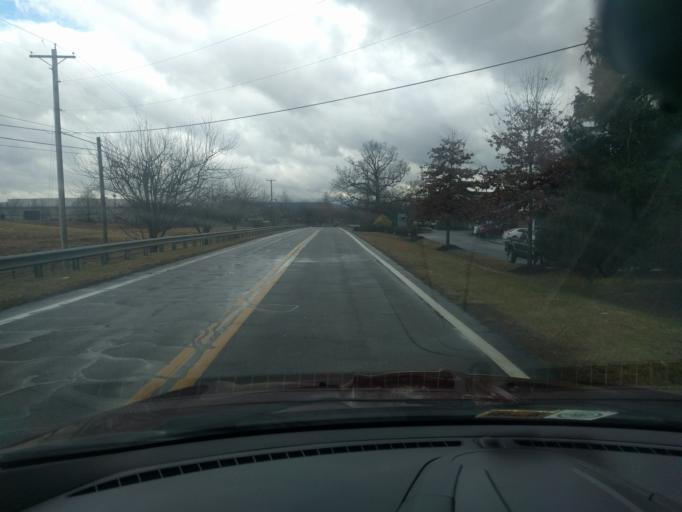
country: US
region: Virginia
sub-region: Roanoke County
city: Hollins
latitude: 37.3168
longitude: -79.9793
